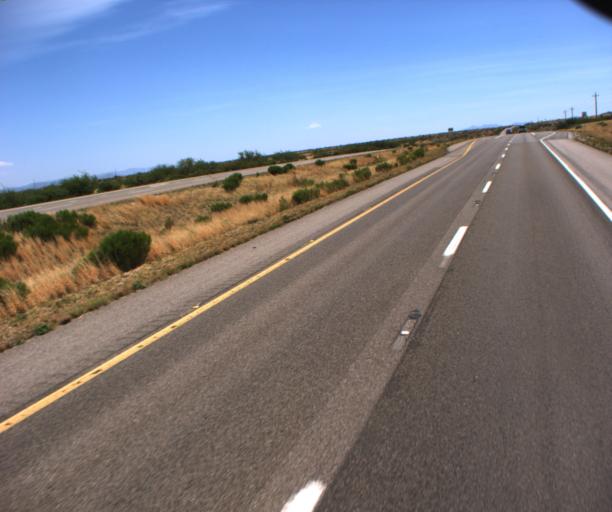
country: US
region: Arizona
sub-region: Cochise County
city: Whetstone
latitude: 31.9437
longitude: -110.3413
